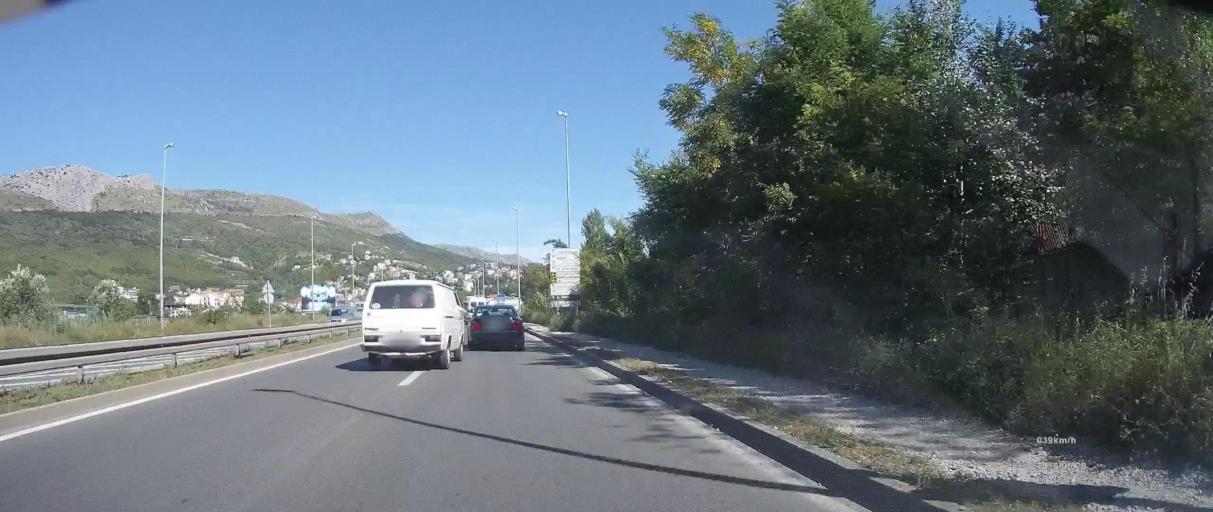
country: HR
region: Splitsko-Dalmatinska
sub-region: Grad Split
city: Stobrec
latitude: 43.5054
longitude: 16.5294
